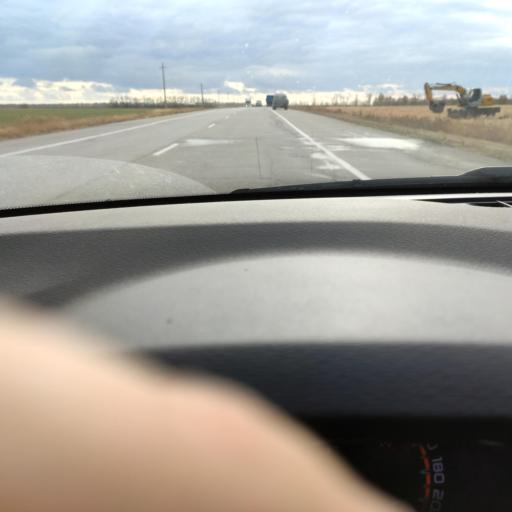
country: RU
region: Voronezj
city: Devitsa
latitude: 51.5664
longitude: 38.9738
